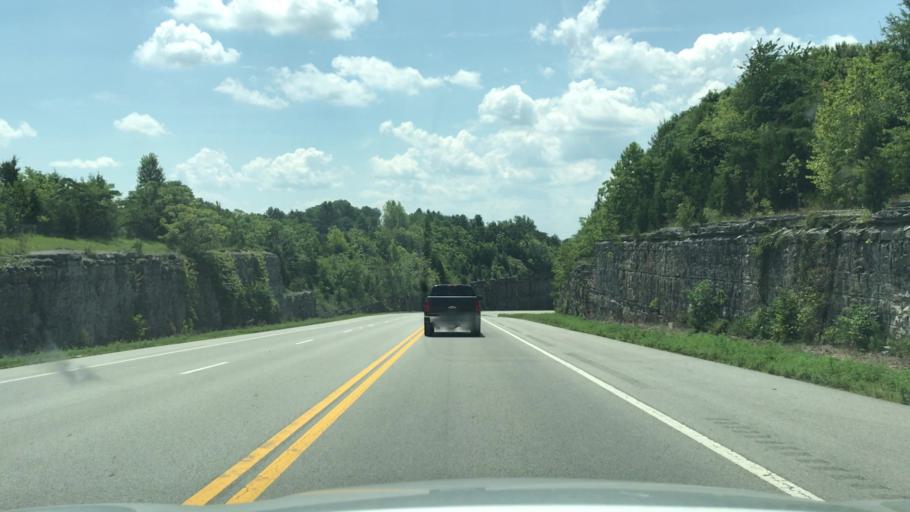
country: US
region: Tennessee
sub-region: Pickett County
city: Byrdstown
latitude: 36.5414
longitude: -85.1609
